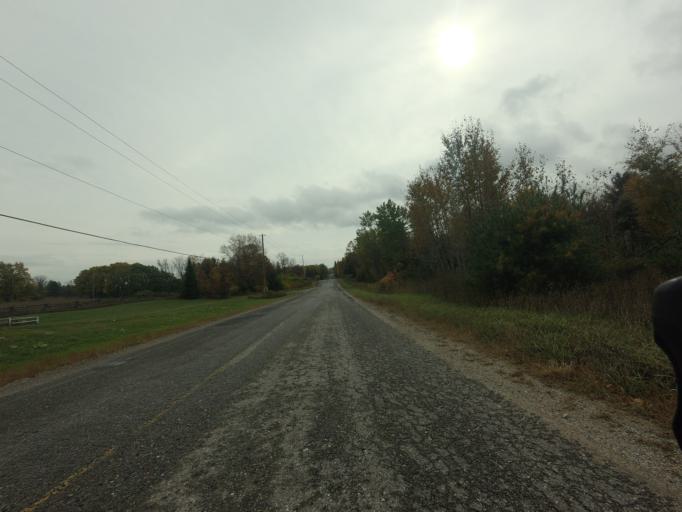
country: CA
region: Ontario
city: Perth
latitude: 45.1206
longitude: -76.5190
